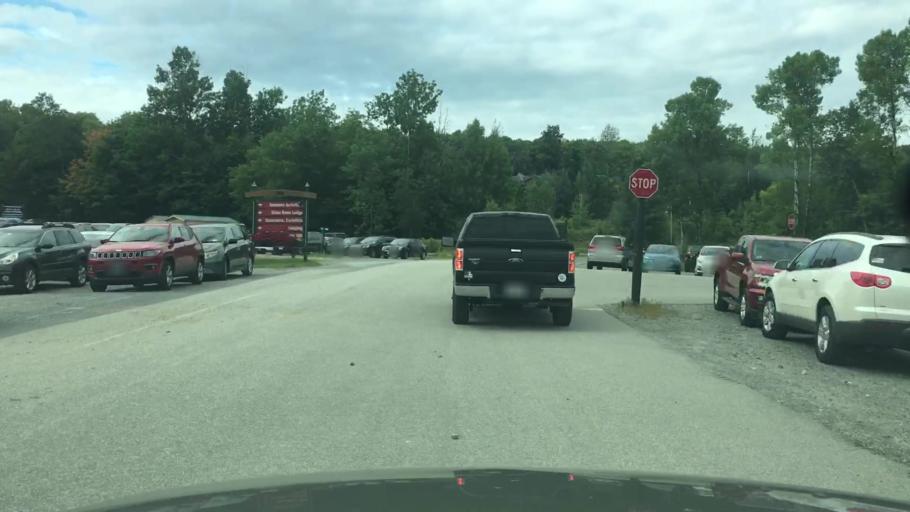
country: US
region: Vermont
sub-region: Windham County
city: Dover
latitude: 42.9702
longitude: -72.8970
